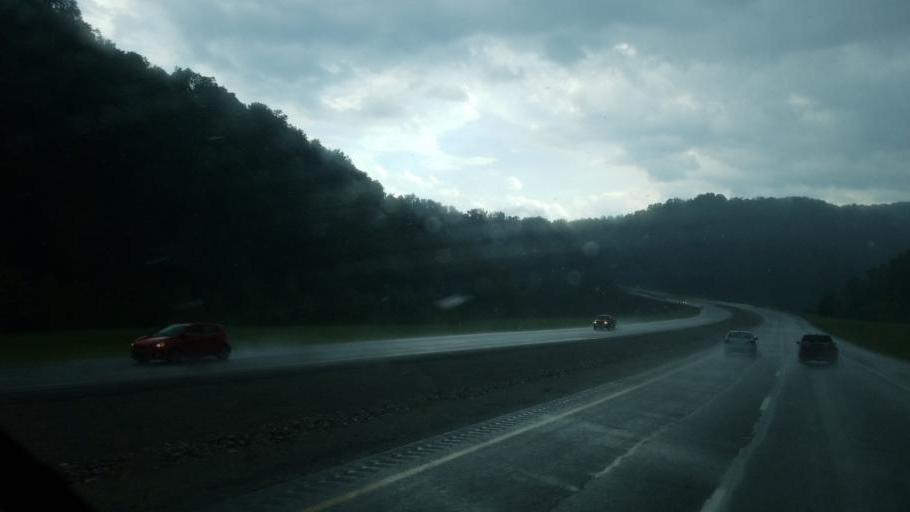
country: US
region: Kentucky
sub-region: Pike County
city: Pikeville
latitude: 37.5463
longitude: -82.4427
